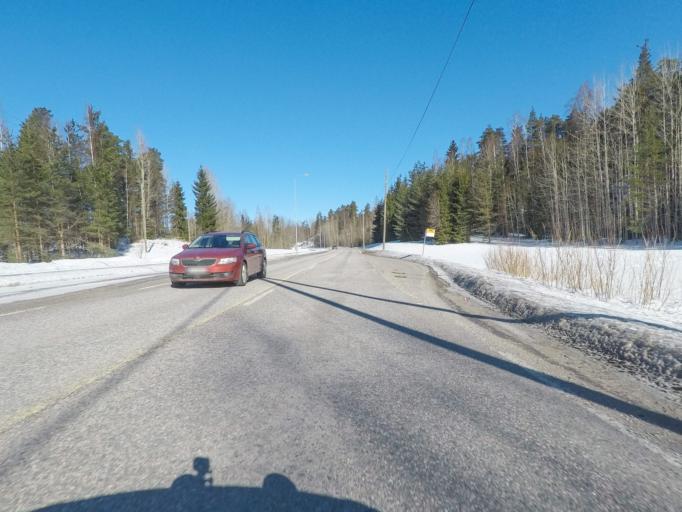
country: FI
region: Uusimaa
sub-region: Helsinki
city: Espoo
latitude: 60.2631
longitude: 24.5994
